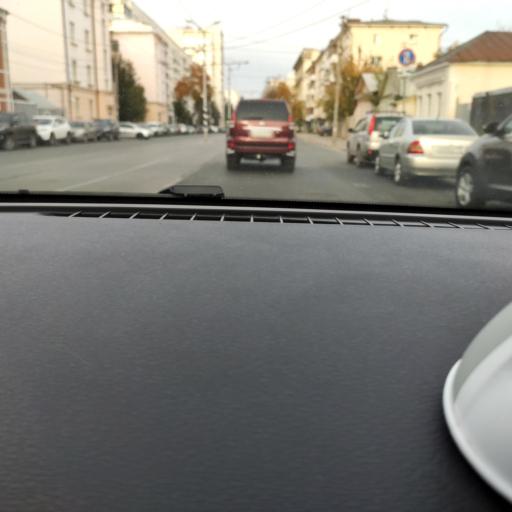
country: RU
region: Samara
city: Samara
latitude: 53.1998
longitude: 50.1086
